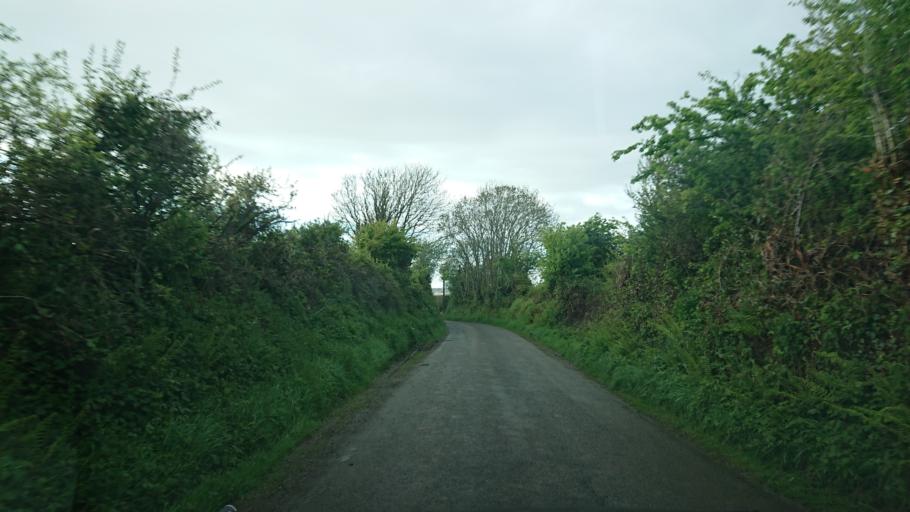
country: IE
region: Munster
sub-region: Waterford
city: Waterford
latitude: 52.2349
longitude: -7.1311
